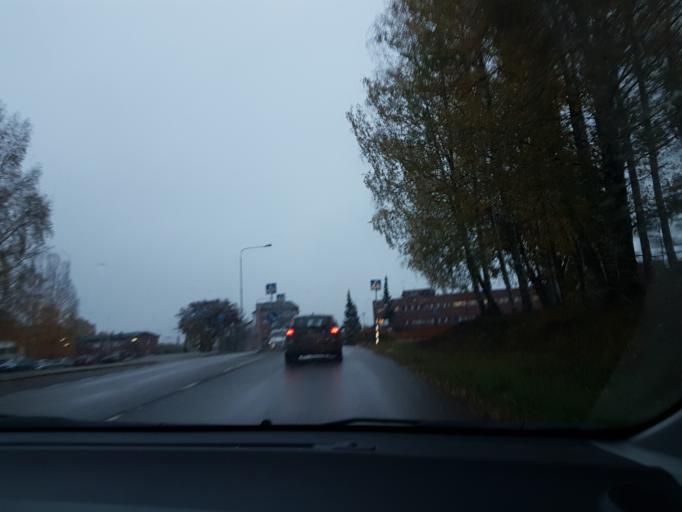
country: FI
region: Uusimaa
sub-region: Helsinki
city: Tuusula
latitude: 60.4035
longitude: 25.0229
